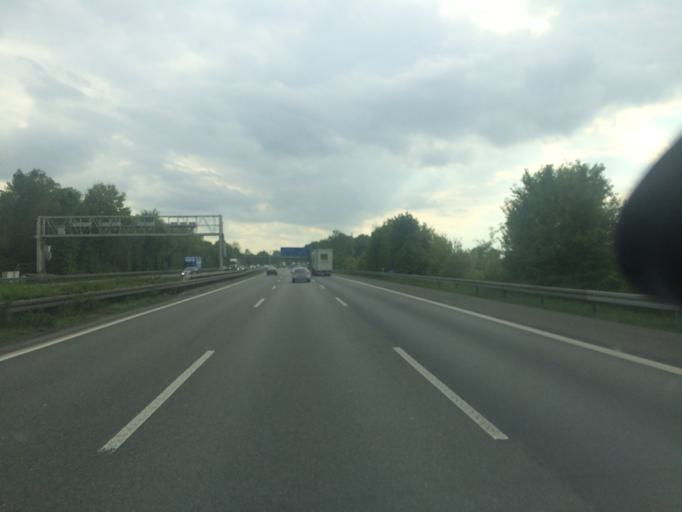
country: DE
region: North Rhine-Westphalia
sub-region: Regierungsbezirk Detmold
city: Guetersloh
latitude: 51.8900
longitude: 8.4452
